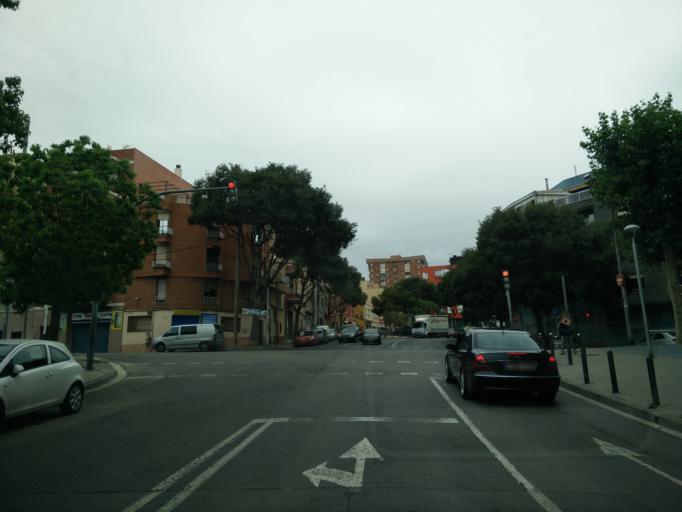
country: ES
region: Catalonia
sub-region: Provincia de Barcelona
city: Llefia
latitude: 41.4522
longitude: 2.2235
